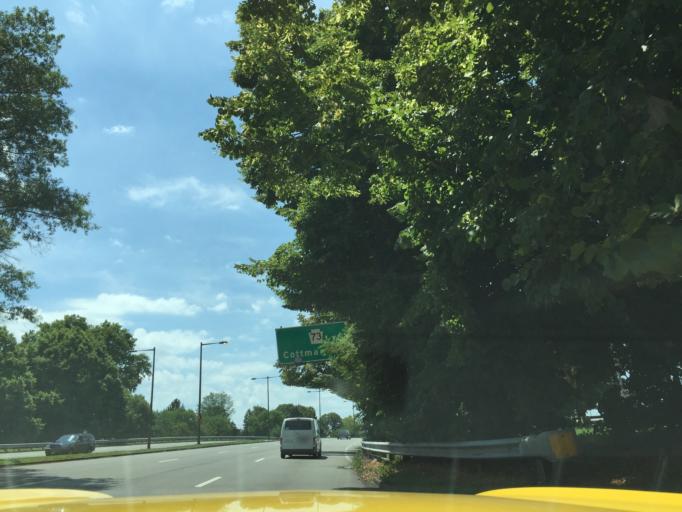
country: US
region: New Jersey
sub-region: Burlington County
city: Palmyra
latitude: 40.0475
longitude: -75.0517
